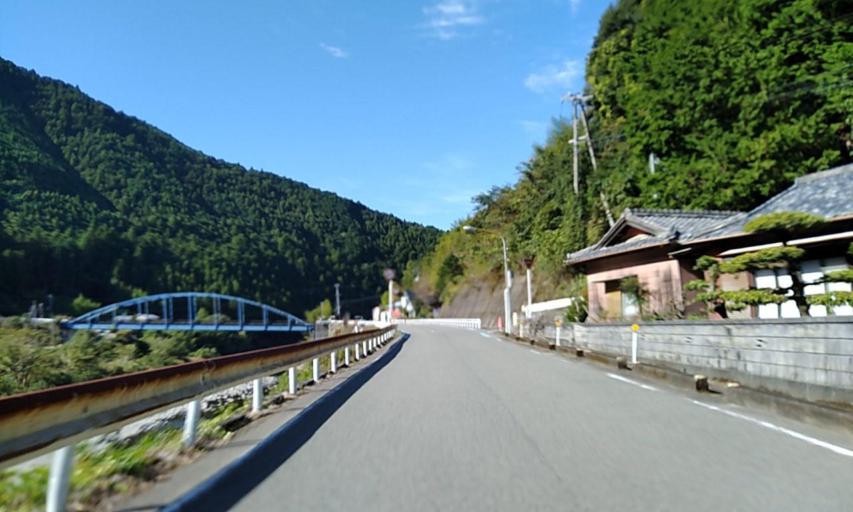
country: JP
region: Wakayama
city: Kainan
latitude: 34.0475
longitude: 135.3416
